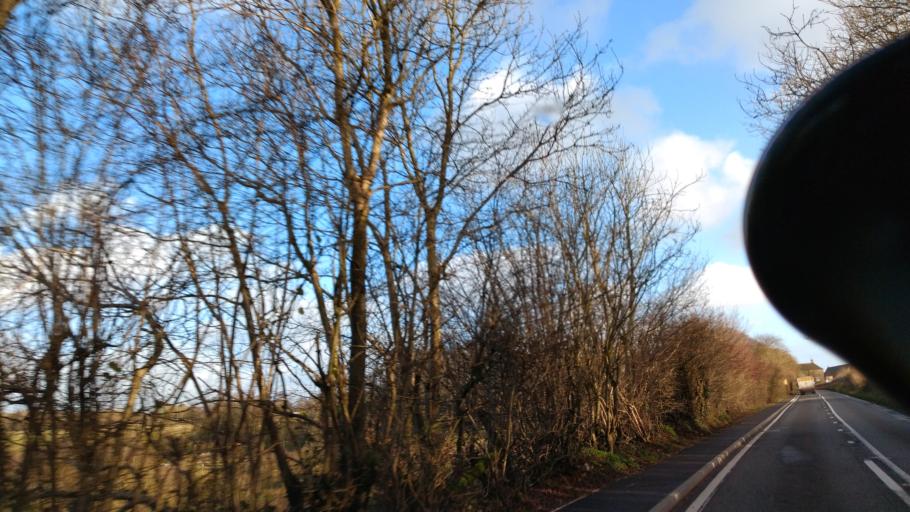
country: GB
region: England
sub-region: Somerset
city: Shepton Mallet
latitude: 51.1863
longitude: -2.5123
